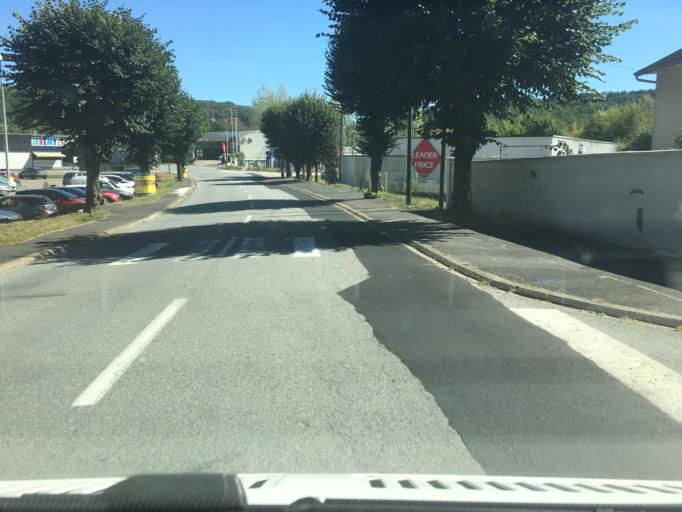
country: FR
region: Limousin
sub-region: Departement de la Correze
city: Bort-les-Orgues
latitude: 45.3944
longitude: 2.4920
